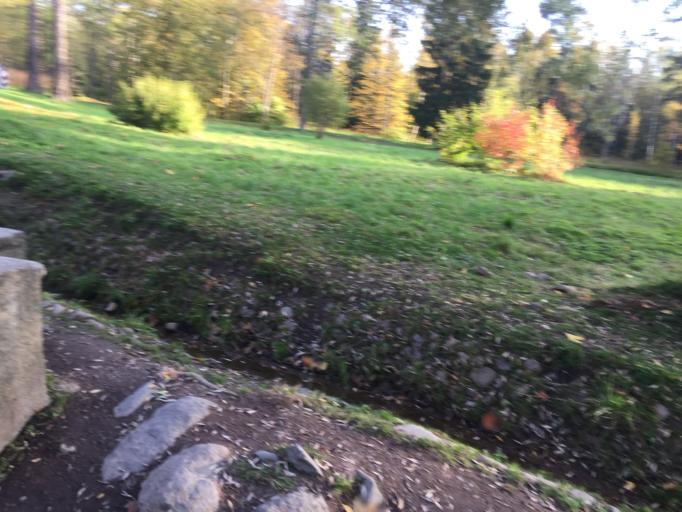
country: RU
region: St.-Petersburg
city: Pushkin
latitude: 59.7217
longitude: 30.3763
